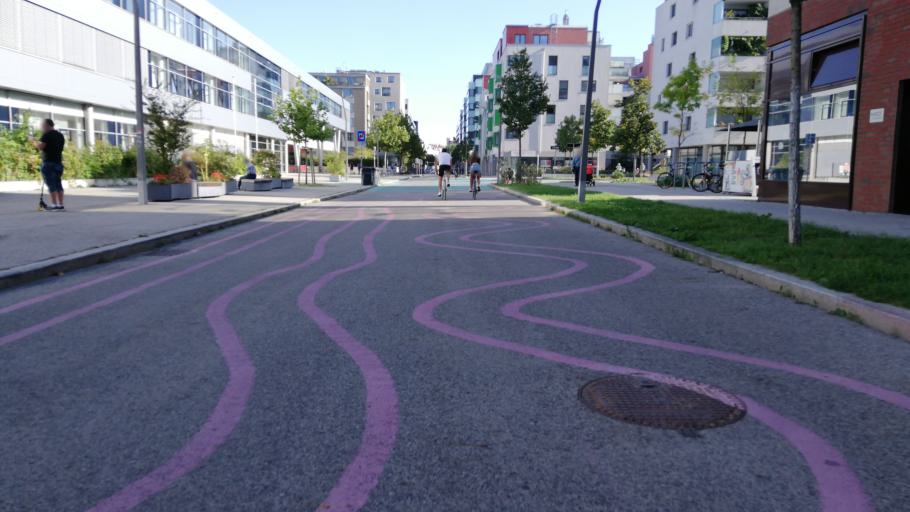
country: AT
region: Vienna
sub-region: Wien Stadt
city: Vienna
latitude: 48.2256
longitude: 16.3948
